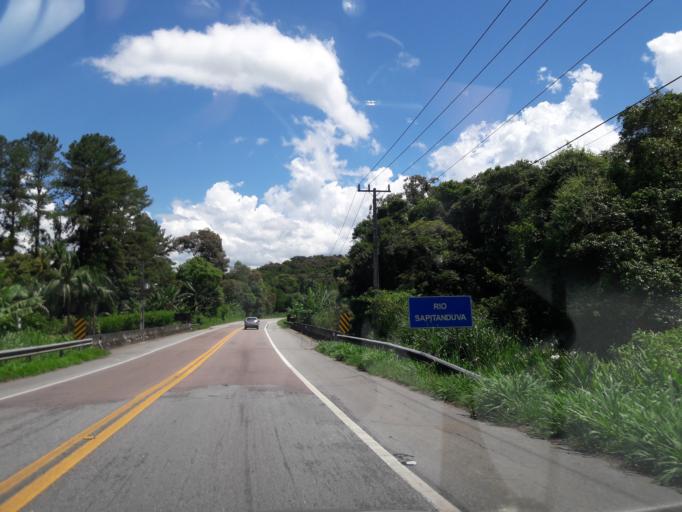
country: BR
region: Parana
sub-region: Antonina
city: Antonina
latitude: -25.4557
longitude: -48.8085
